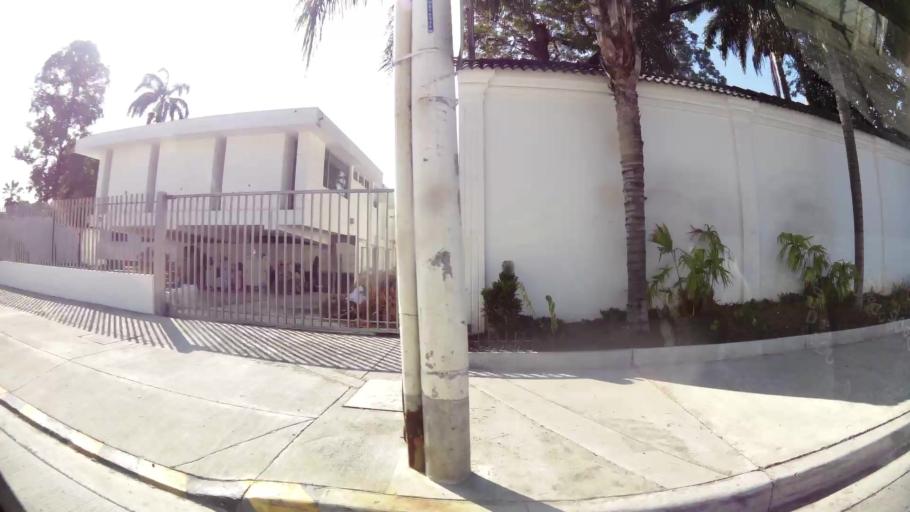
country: EC
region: Guayas
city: Guayaquil
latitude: -2.1702
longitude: -79.9027
